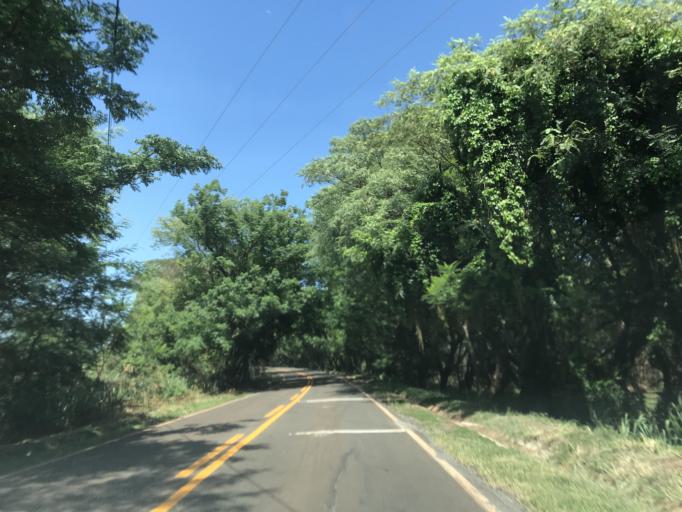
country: BR
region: Parana
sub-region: Terra Rica
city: Terra Rica
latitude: -22.7752
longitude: -52.6534
